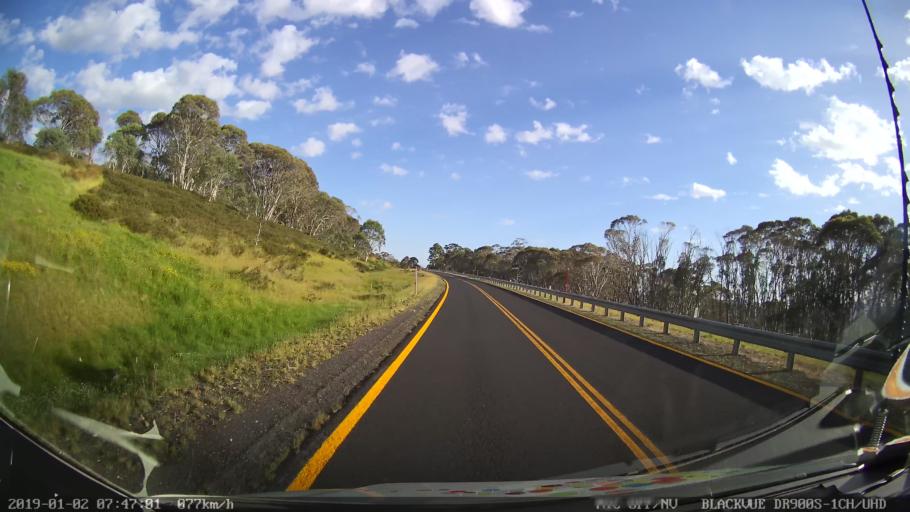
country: AU
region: New South Wales
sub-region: Tumut Shire
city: Tumut
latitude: -35.7694
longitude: 148.5214
